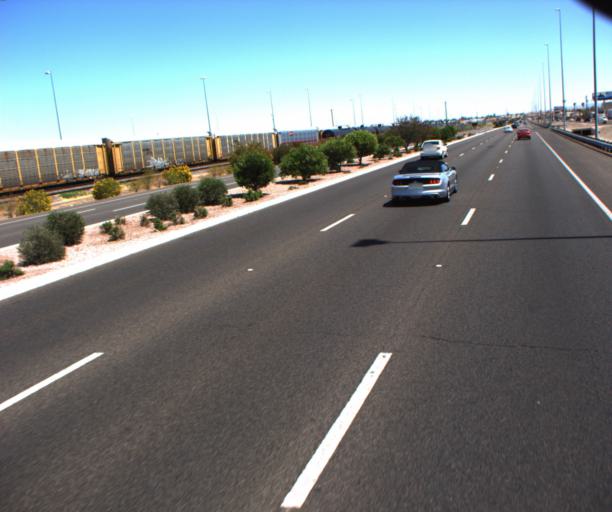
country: US
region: Arizona
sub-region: Maricopa County
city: El Mirage
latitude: 33.6206
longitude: -112.3272
